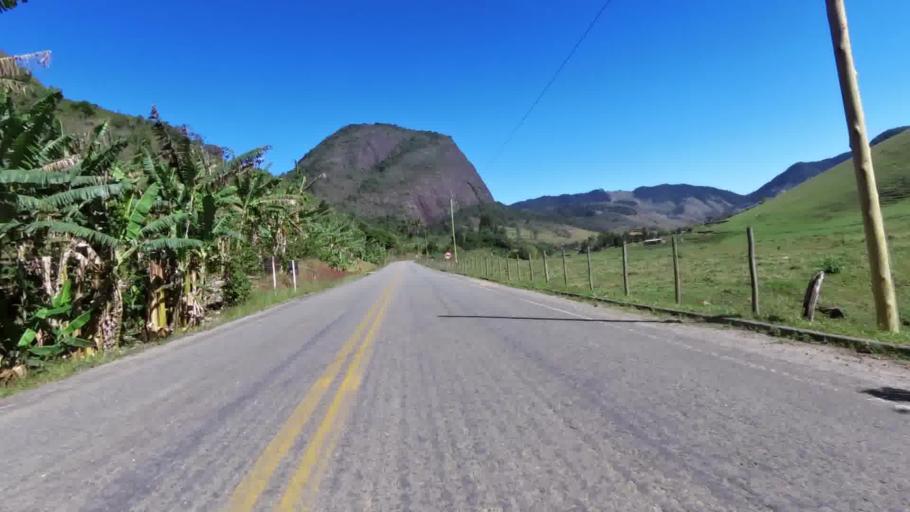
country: BR
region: Espirito Santo
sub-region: Iconha
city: Iconha
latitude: -20.7199
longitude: -40.8993
